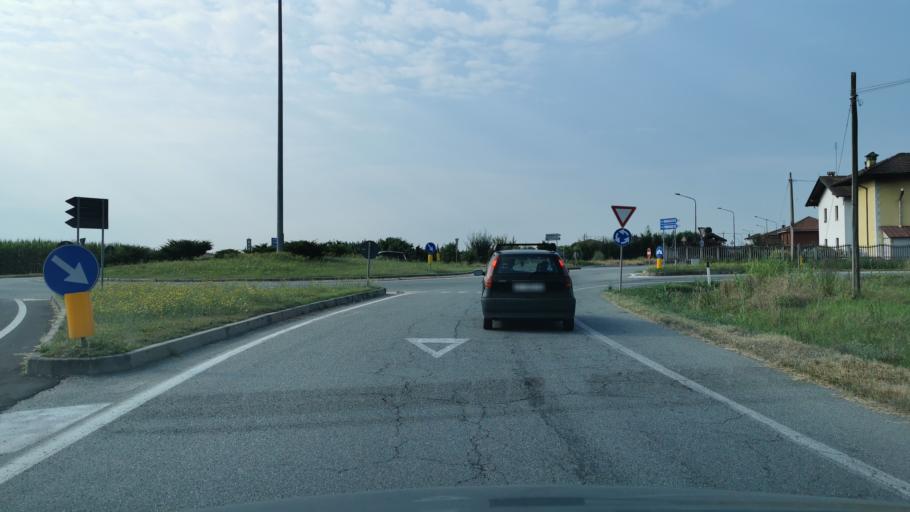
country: IT
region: Piedmont
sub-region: Provincia di Torino
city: Cercenasco
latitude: 44.8671
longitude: 7.4977
